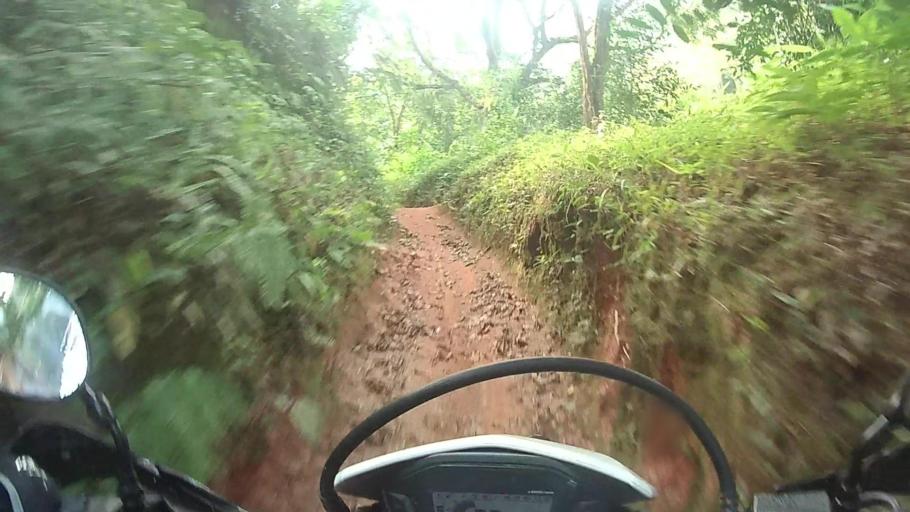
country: TH
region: Lampang
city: Mueang Pan
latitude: 18.7999
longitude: 99.3821
